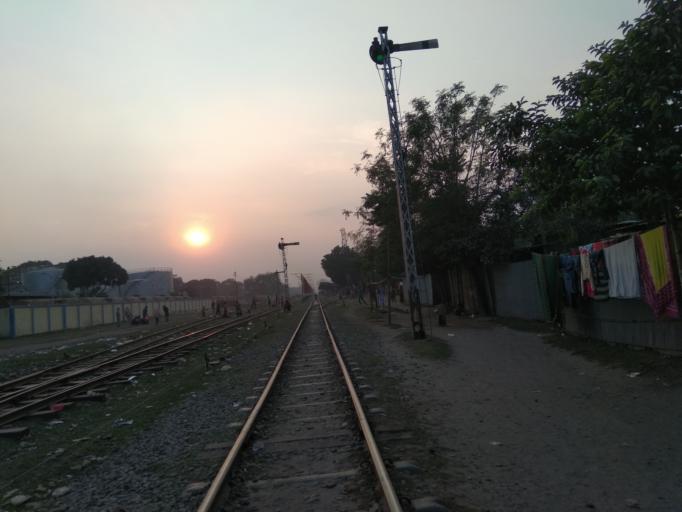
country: BD
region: Rangpur Division
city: Rangpur
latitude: 25.7292
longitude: 89.2664
